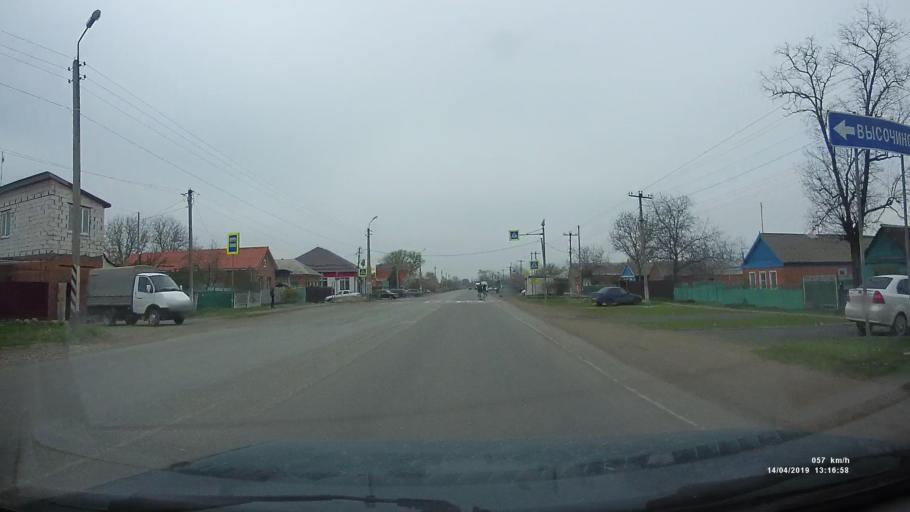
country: RU
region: Rostov
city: Kuleshovka
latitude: 47.0791
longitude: 39.5728
